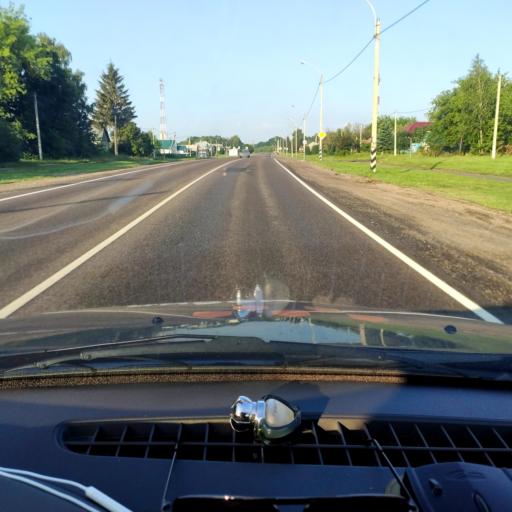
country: RU
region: Lipetsk
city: Kazaki
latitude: 52.6200
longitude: 38.2676
